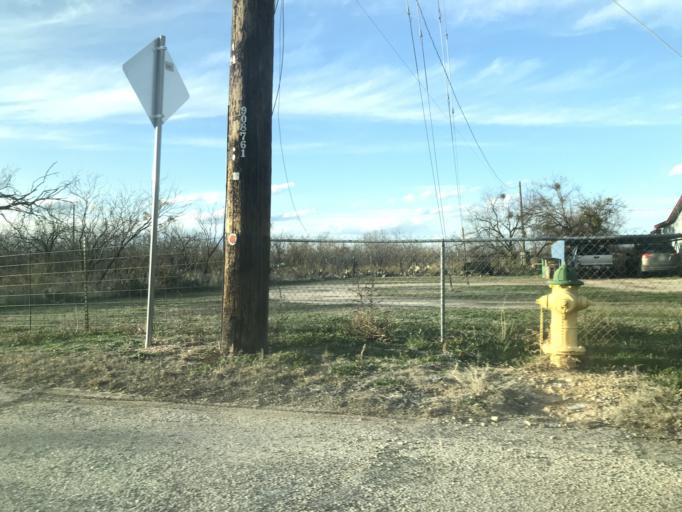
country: US
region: Texas
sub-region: Tom Green County
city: San Angelo
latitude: 31.4973
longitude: -100.4427
